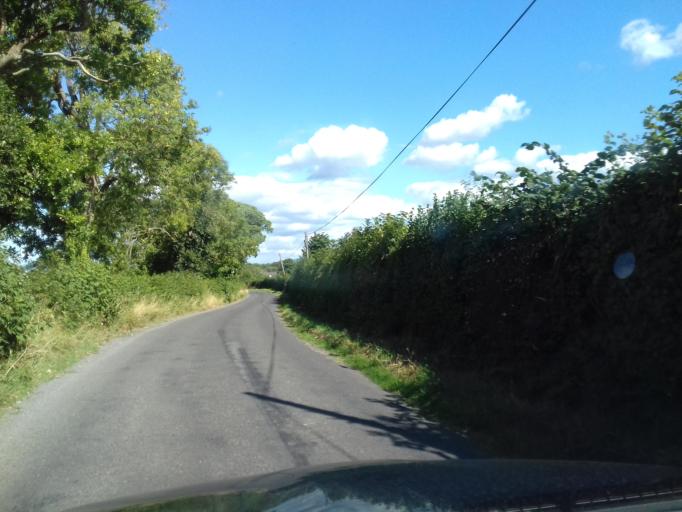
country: IE
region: Leinster
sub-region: Kilkenny
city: Callan
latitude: 52.5385
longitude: -7.3001
